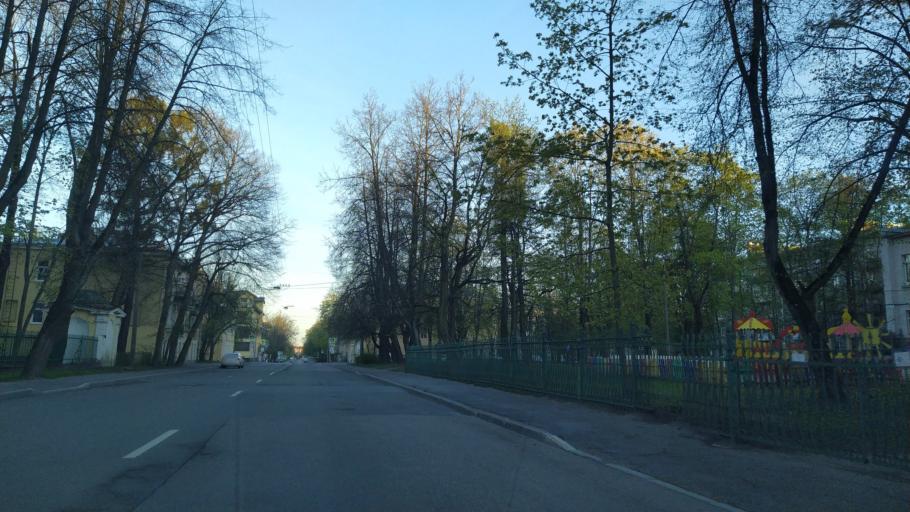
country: RU
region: St.-Petersburg
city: Pushkin
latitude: 59.7101
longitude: 30.4073
